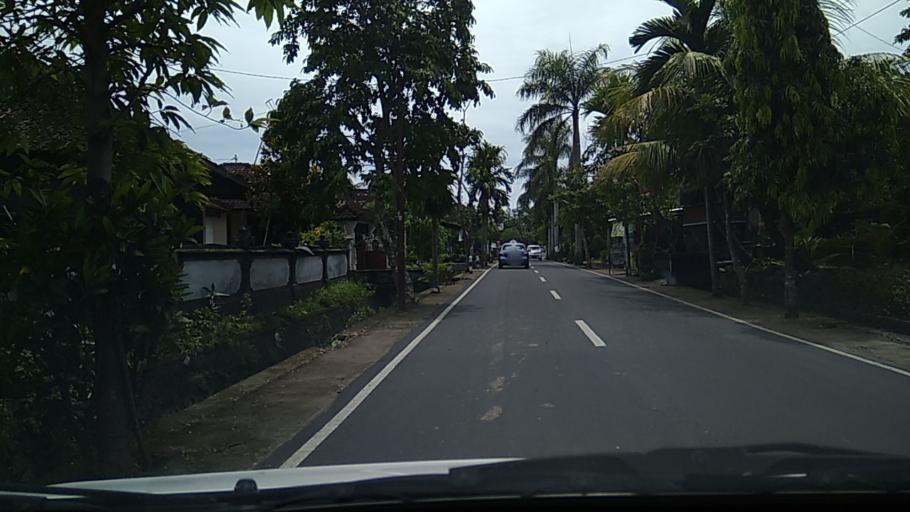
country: ID
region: Bali
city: Banjar Batanbuah
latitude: -8.6103
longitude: 115.0996
